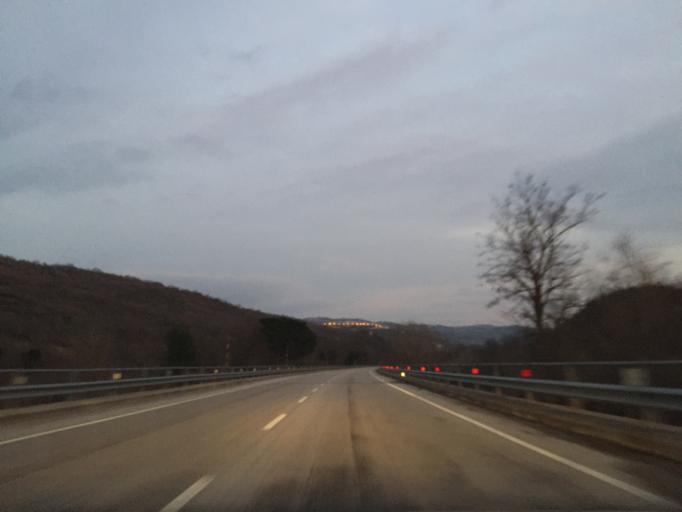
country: IT
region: Apulia
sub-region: Provincia di Foggia
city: San Marco la Catola
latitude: 41.5028
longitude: 15.0223
